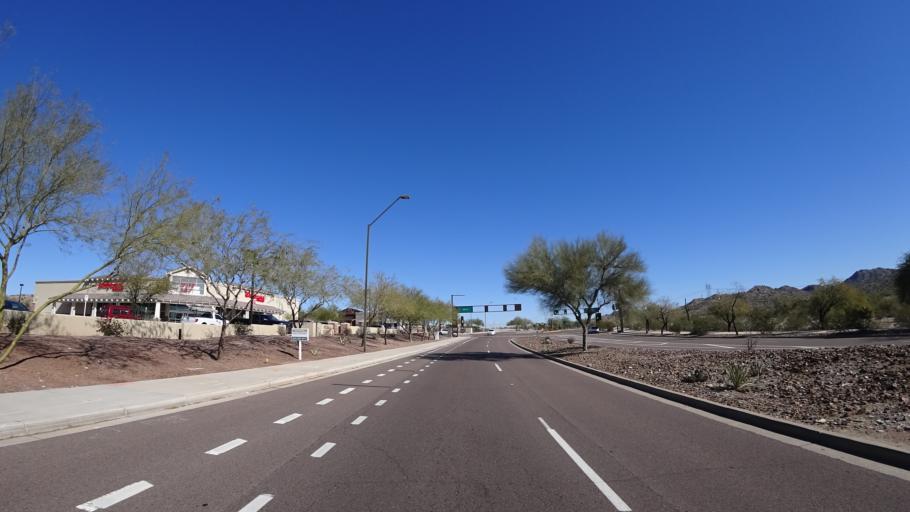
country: US
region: Arizona
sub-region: Maricopa County
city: Goodyear
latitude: 33.3570
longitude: -112.4265
